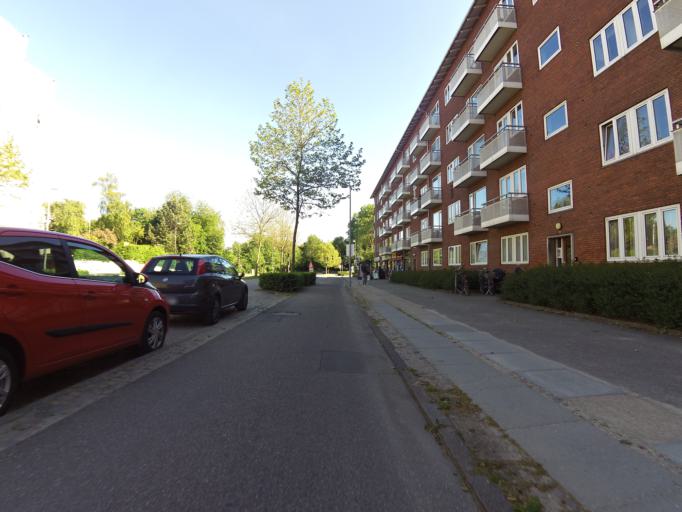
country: DK
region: Capital Region
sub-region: Lyngby-Tarbaek Kommune
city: Kongens Lyngby
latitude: 55.7640
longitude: 12.5110
